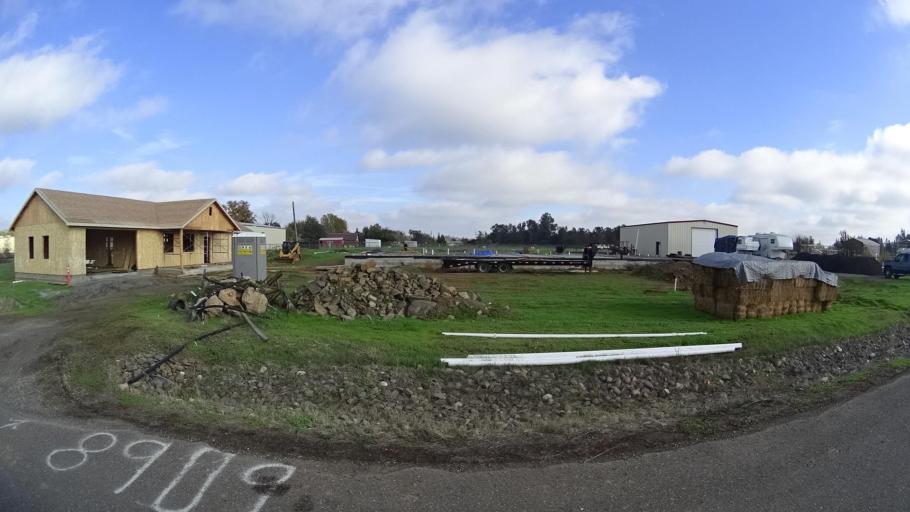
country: US
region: California
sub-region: Sacramento County
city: Vineyard
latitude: 38.4335
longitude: -121.3405
